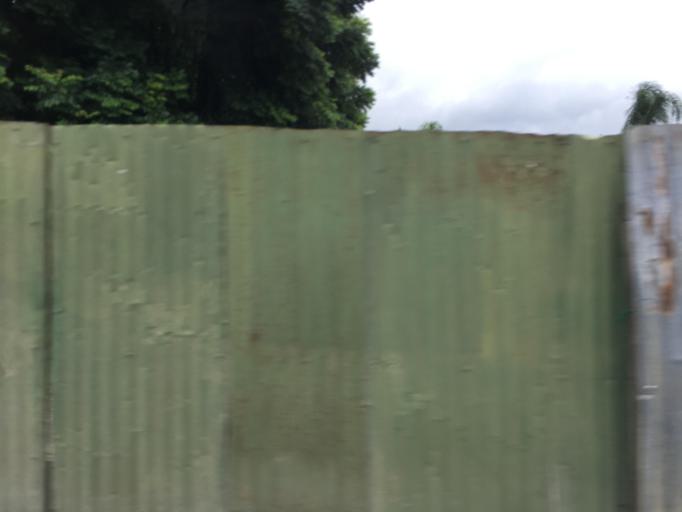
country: GT
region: Sacatepequez
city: Jocotenango
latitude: 14.5806
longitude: -90.7462
